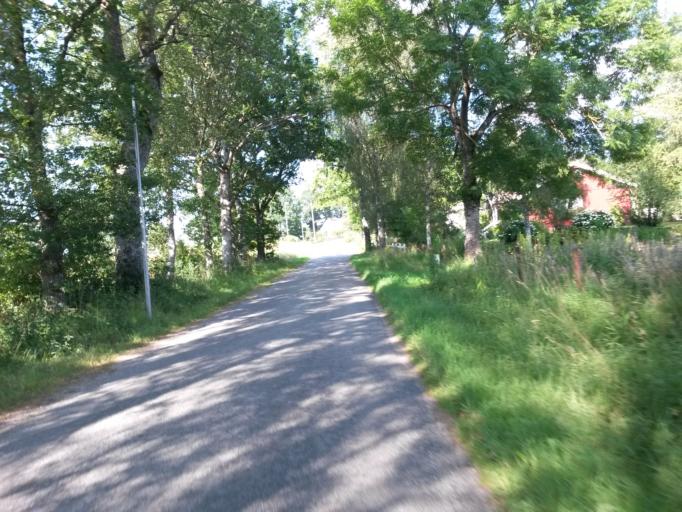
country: SE
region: Vaestra Goetaland
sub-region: Vargarda Kommun
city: Jonstorp
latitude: 58.0105
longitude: 12.7092
